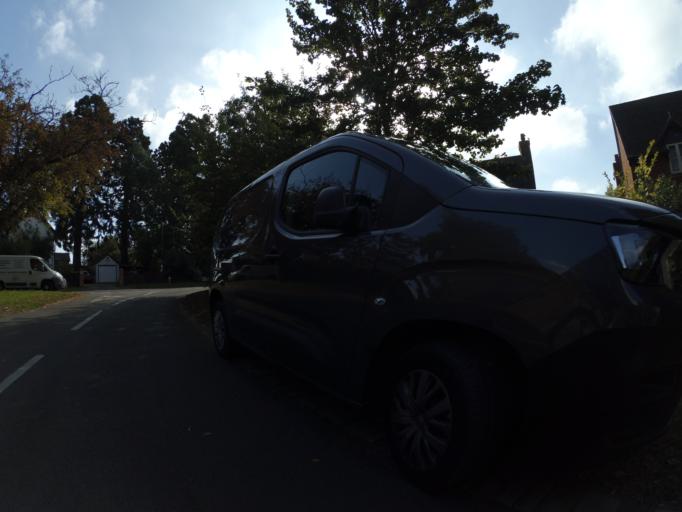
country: GB
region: England
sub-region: Warwickshire
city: Rugby
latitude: 52.3809
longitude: -1.2169
